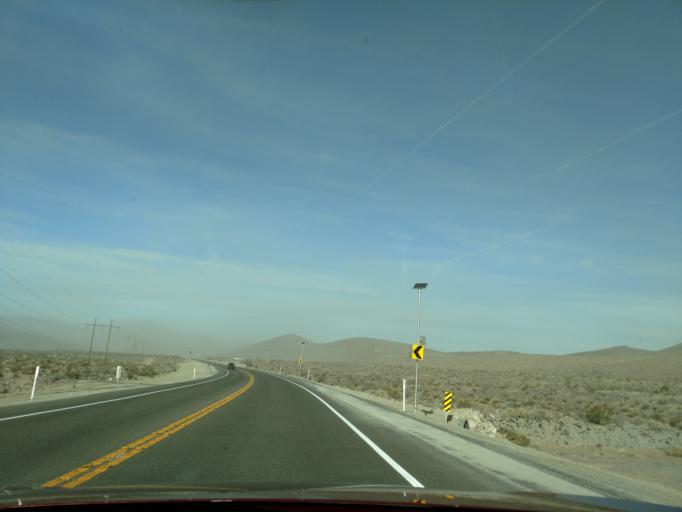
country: US
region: Nevada
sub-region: Nye County
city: Pahrump
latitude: 36.4354
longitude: -116.0752
